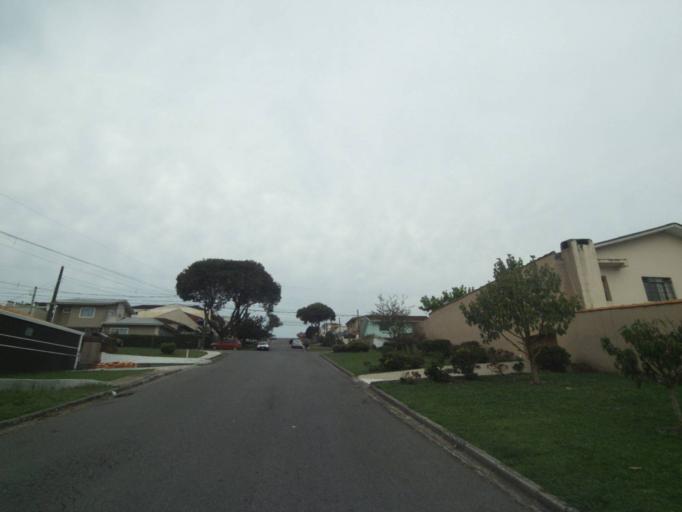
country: BR
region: Parana
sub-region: Pinhais
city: Pinhais
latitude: -25.4028
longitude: -49.2044
